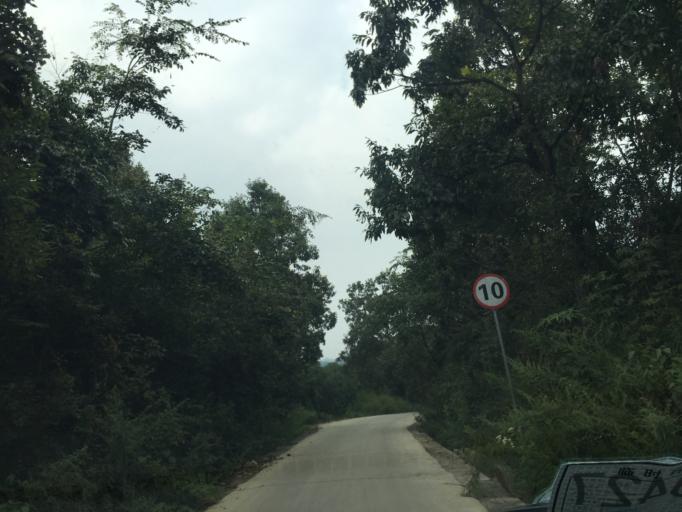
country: CN
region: Guangxi Zhuangzu Zizhiqu
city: Xinzhou
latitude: 25.5650
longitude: 105.6035
